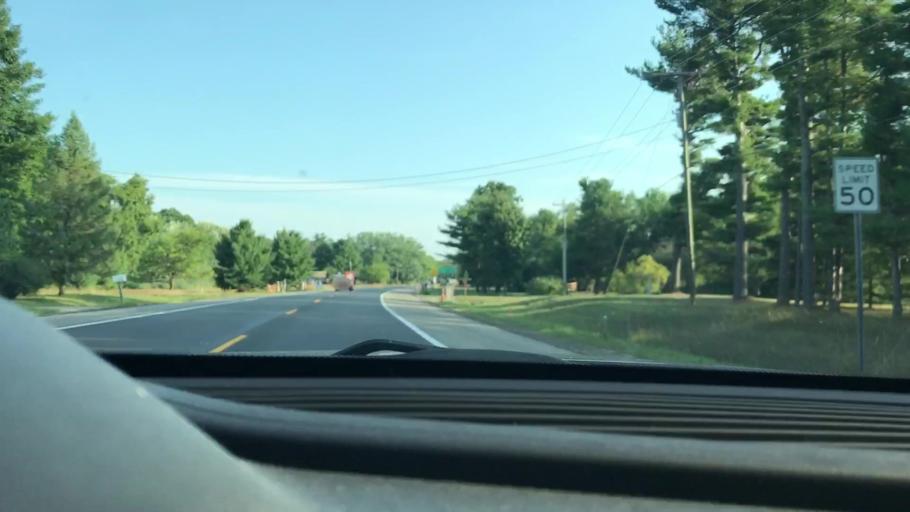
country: US
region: Michigan
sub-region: Antrim County
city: Bellaire
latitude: 45.0701
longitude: -85.3590
